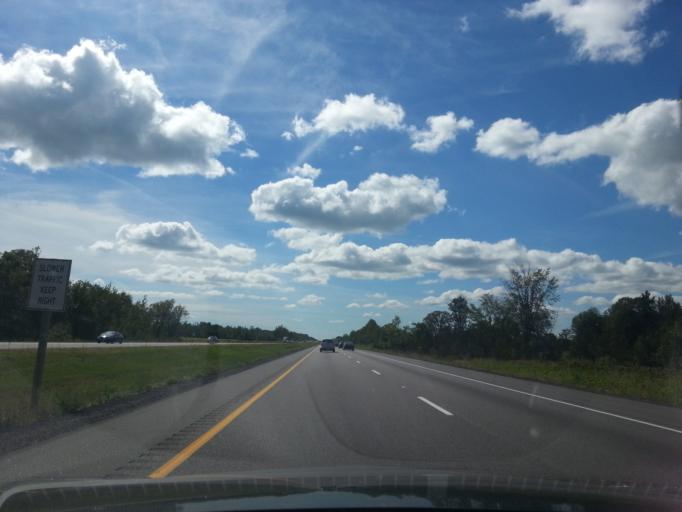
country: CA
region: Ontario
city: Deseronto
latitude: 44.2437
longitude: -77.0696
